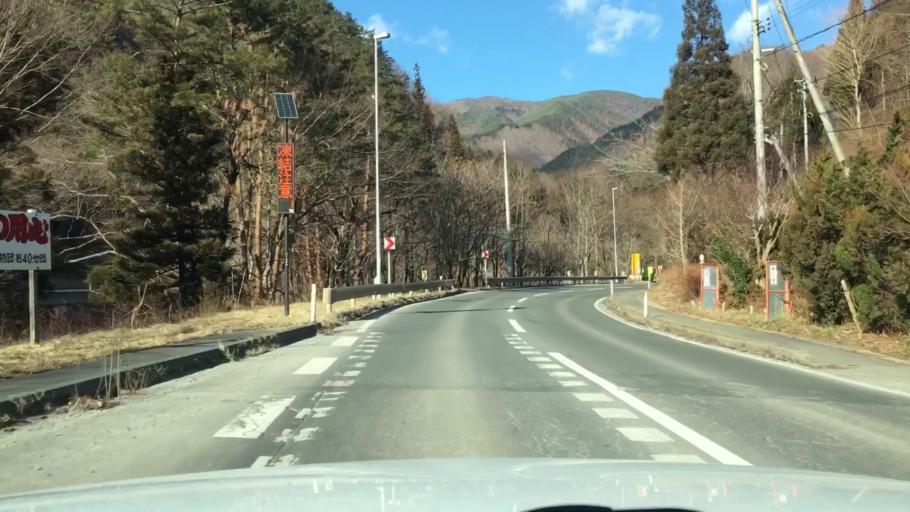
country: JP
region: Iwate
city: Miyako
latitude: 39.6010
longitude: 141.6474
